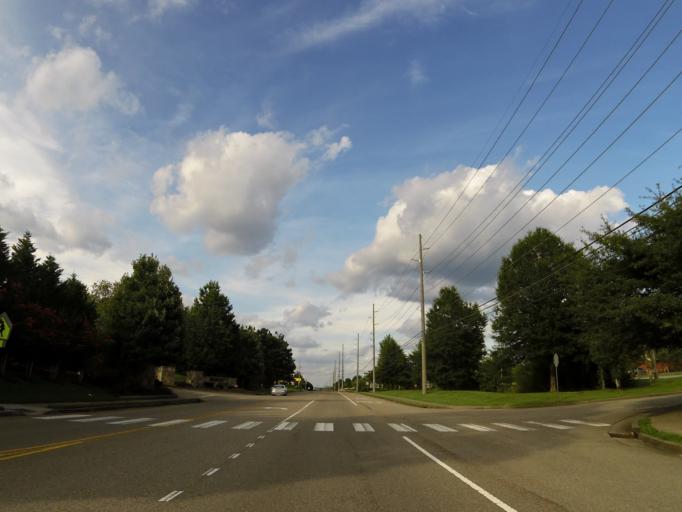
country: US
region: Tennessee
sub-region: Knox County
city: Farragut
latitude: 35.8831
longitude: -84.0853
